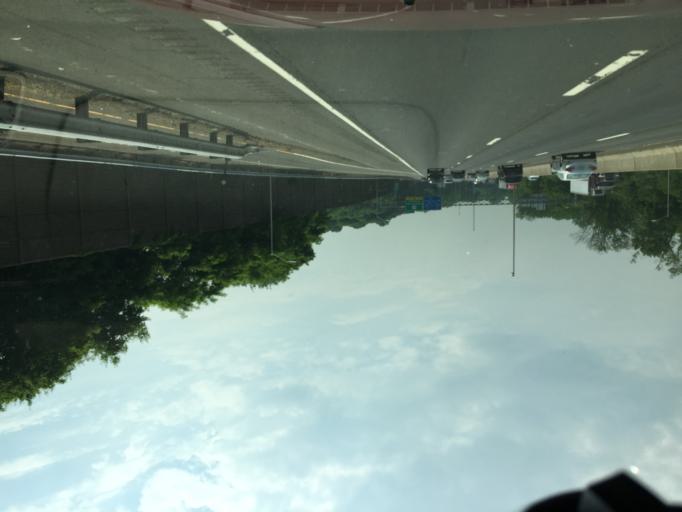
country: US
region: Connecticut
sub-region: Fairfield County
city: Darien
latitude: 41.0730
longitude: -73.4725
